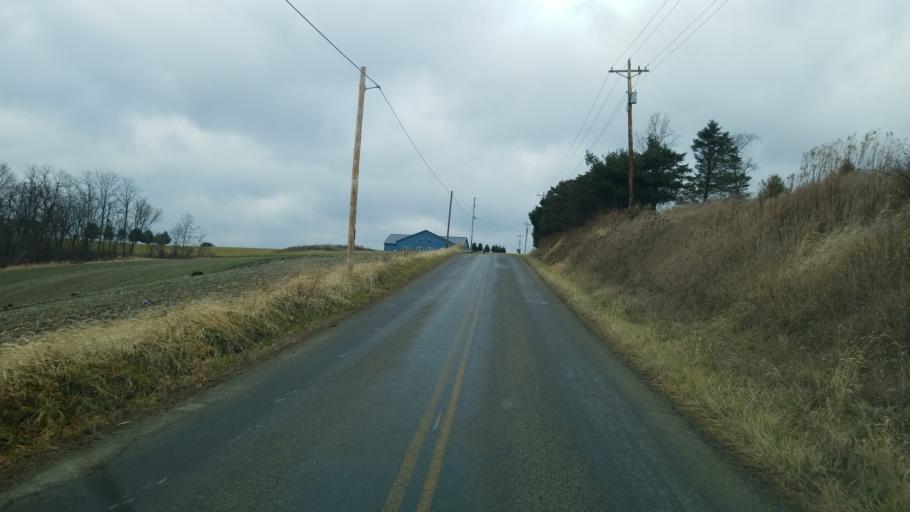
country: US
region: Ohio
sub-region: Holmes County
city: Millersburg
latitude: 40.5736
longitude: -81.9606
